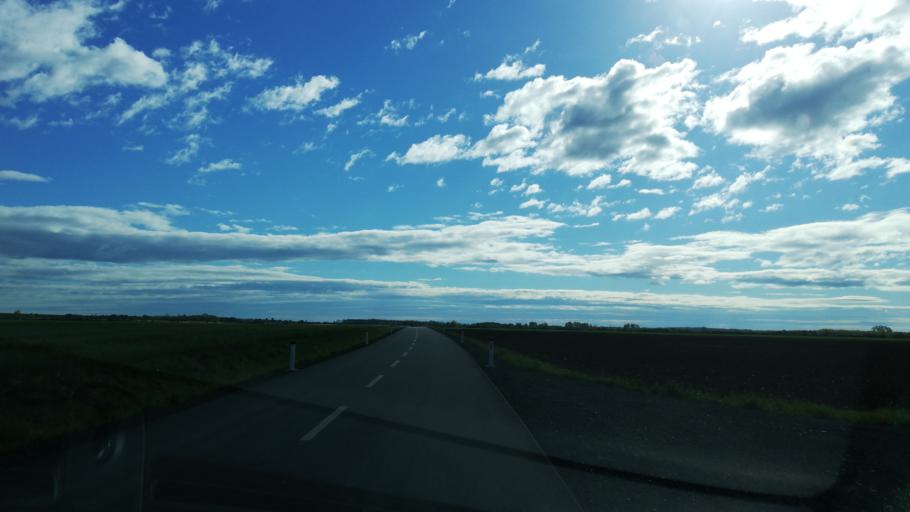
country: AT
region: Burgenland
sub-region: Politischer Bezirk Oberpullendorf
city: Lutzmannsburg
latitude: 47.4695
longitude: 16.6565
